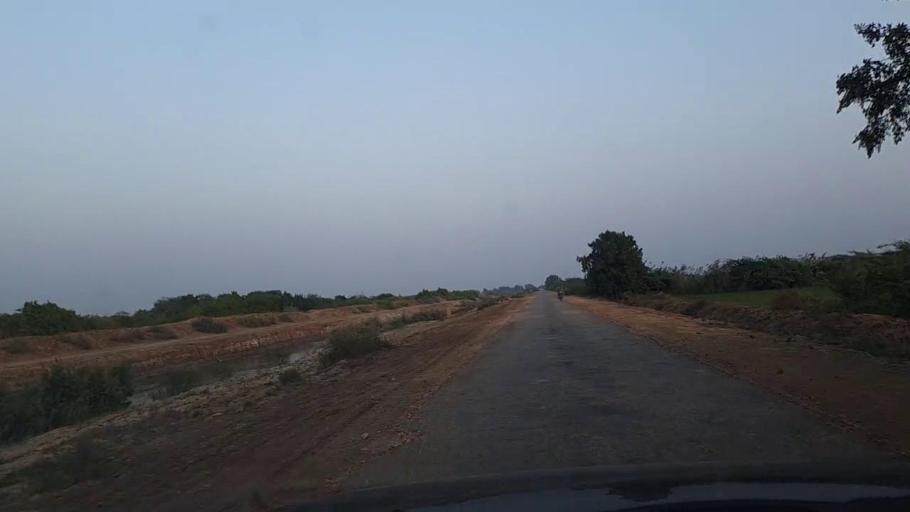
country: PK
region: Sindh
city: Mirpur Sakro
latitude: 24.6303
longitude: 67.6365
